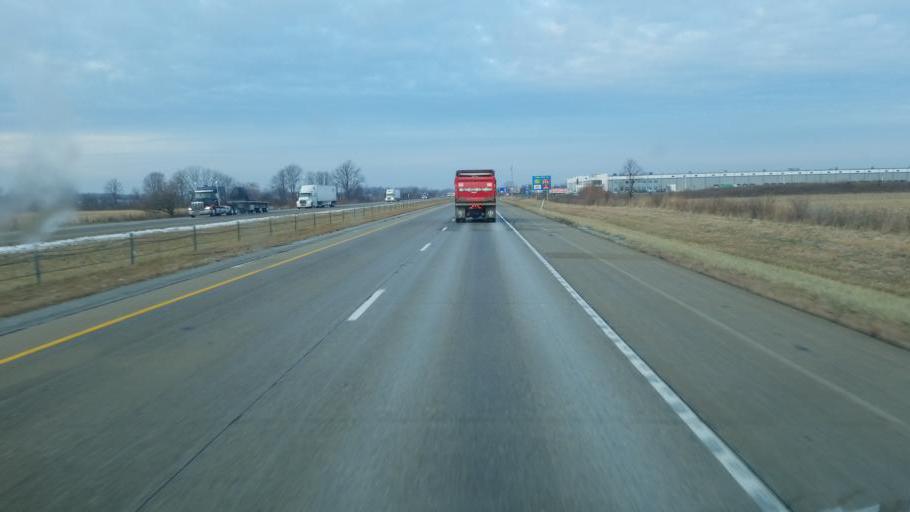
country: US
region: Indiana
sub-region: Marion County
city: Cumberland
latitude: 39.8198
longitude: -85.8791
